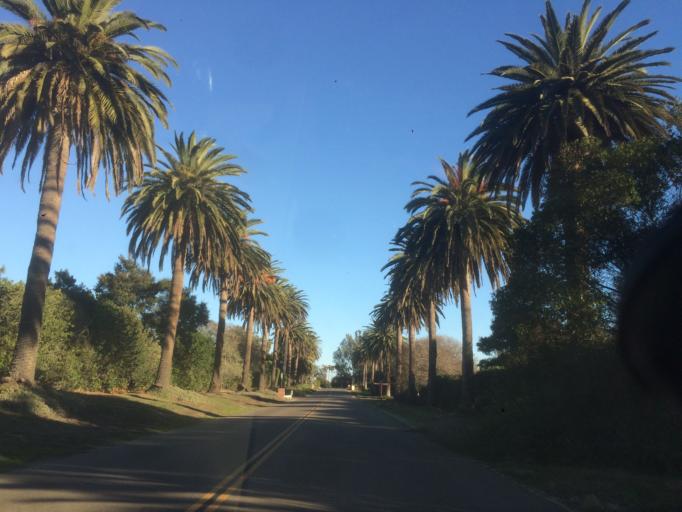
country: US
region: California
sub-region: Santa Barbara County
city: Santa Barbara
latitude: 34.4098
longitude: -119.7585
